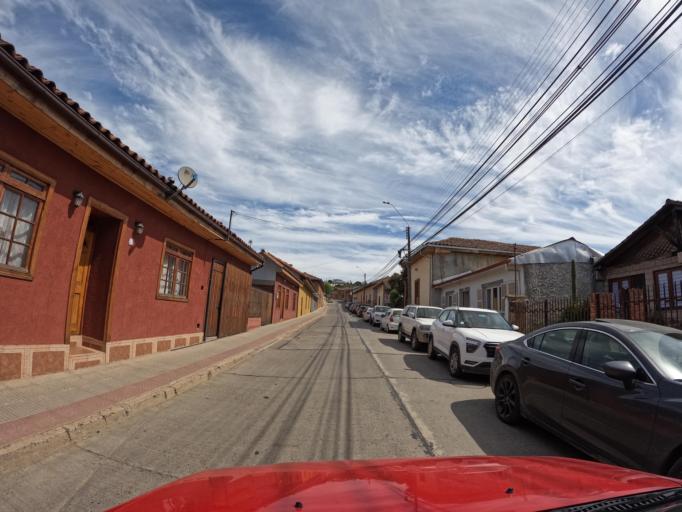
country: CL
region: Maule
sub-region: Provincia de Talca
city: Constitucion
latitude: -35.0951
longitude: -72.0191
